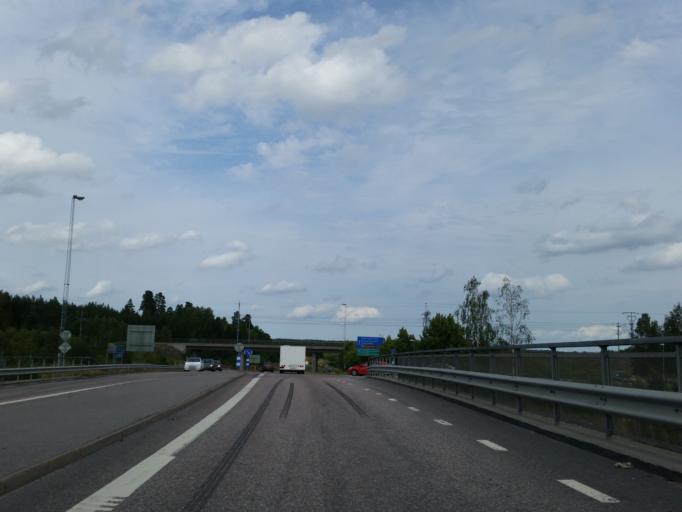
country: SE
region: Soedermanland
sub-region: Strangnas Kommun
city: Mariefred
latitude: 59.2476
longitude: 17.1639
